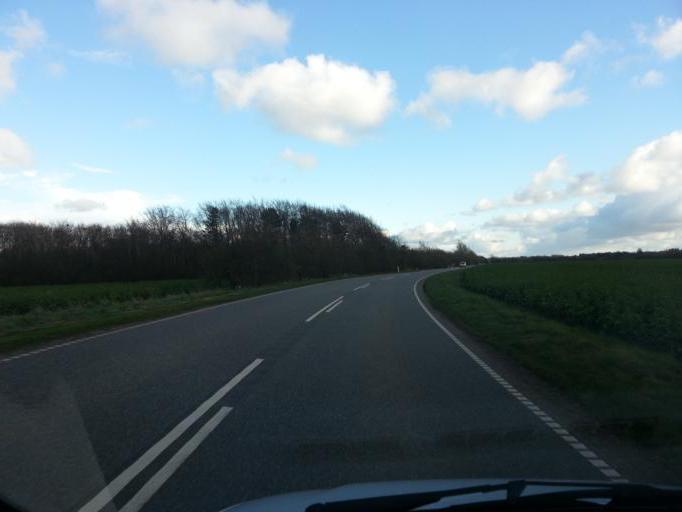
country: DK
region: Central Jutland
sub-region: Ringkobing-Skjern Kommune
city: Tarm
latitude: 55.8842
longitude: 8.5254
